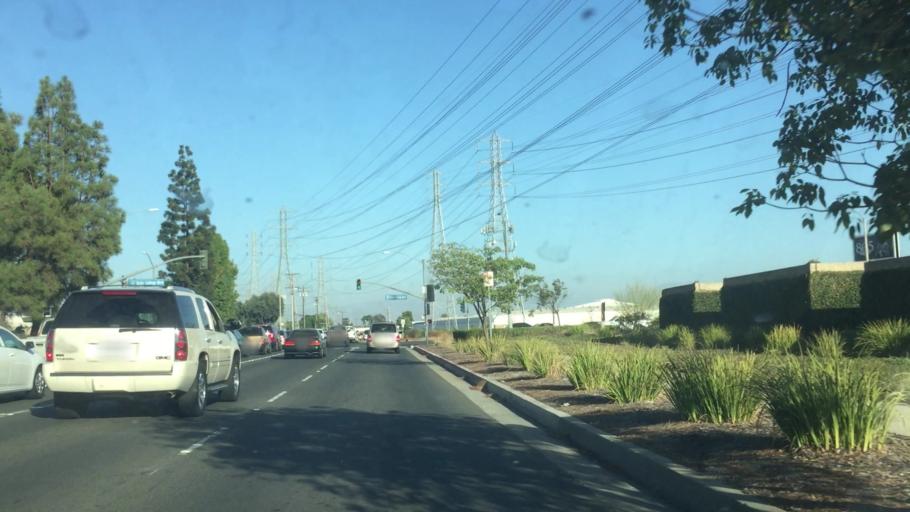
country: US
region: California
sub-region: Orange County
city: Anaheim
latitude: 33.8106
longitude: -117.8901
